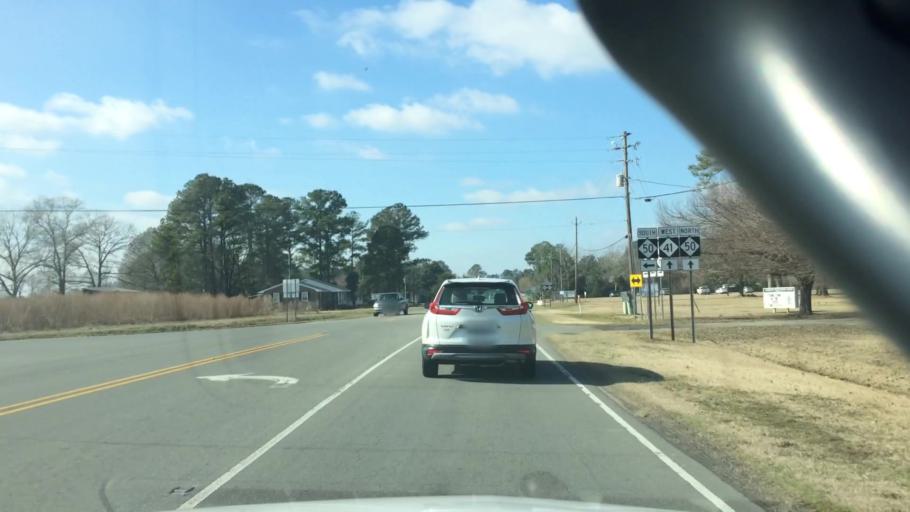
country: US
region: North Carolina
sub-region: Duplin County
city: Beulaville
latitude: 34.8296
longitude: -77.8121
